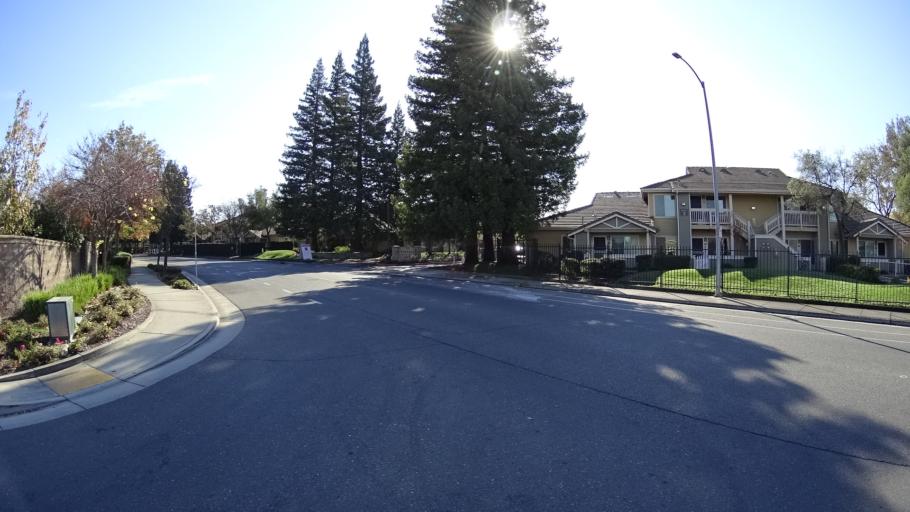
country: US
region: California
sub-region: Sacramento County
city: Citrus Heights
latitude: 38.6822
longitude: -121.2943
